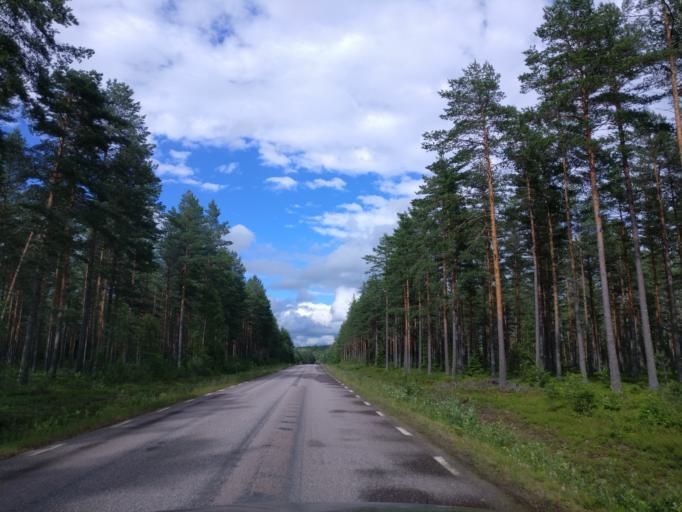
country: SE
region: Vaermland
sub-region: Hagfors Kommun
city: Ekshaerad
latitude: 60.0407
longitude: 13.5150
